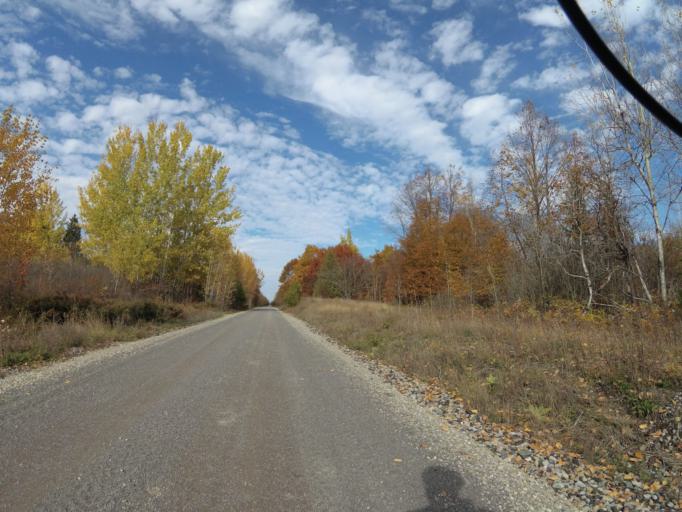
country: CA
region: Ontario
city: Carleton Place
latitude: 45.0632
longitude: -76.0951
